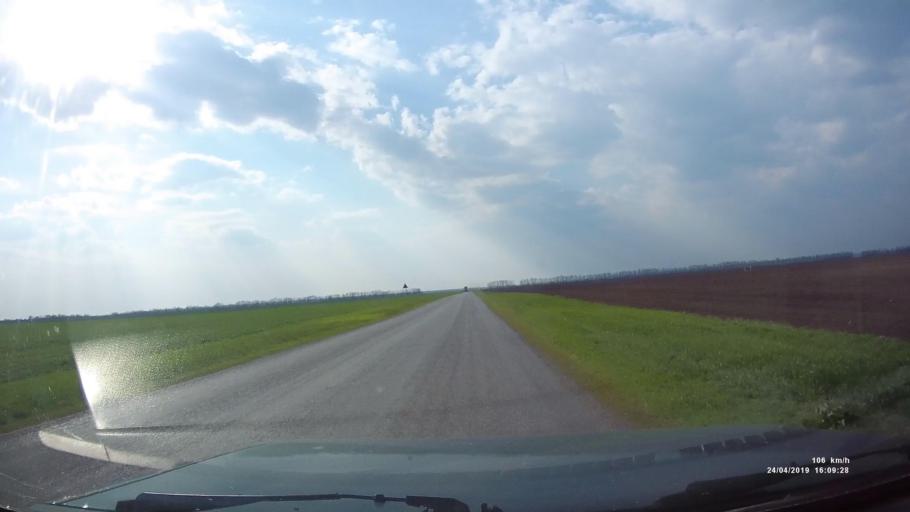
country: RU
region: Rostov
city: Sovetskoye
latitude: 46.7082
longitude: 42.2892
